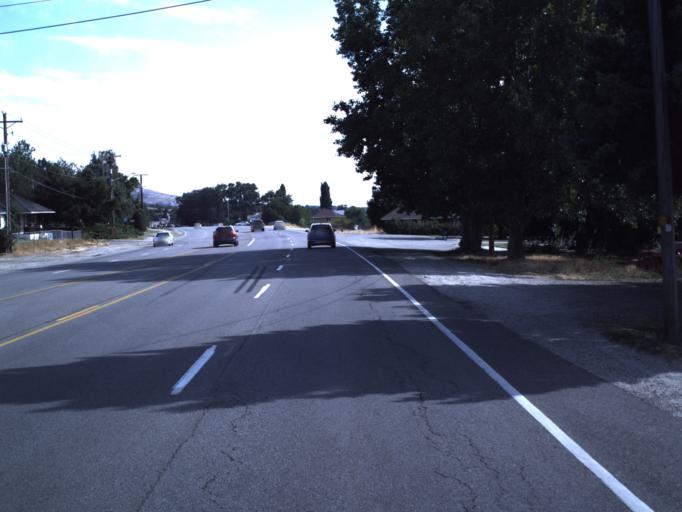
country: US
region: Utah
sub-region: Box Elder County
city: Willard
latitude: 41.4063
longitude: -112.0365
